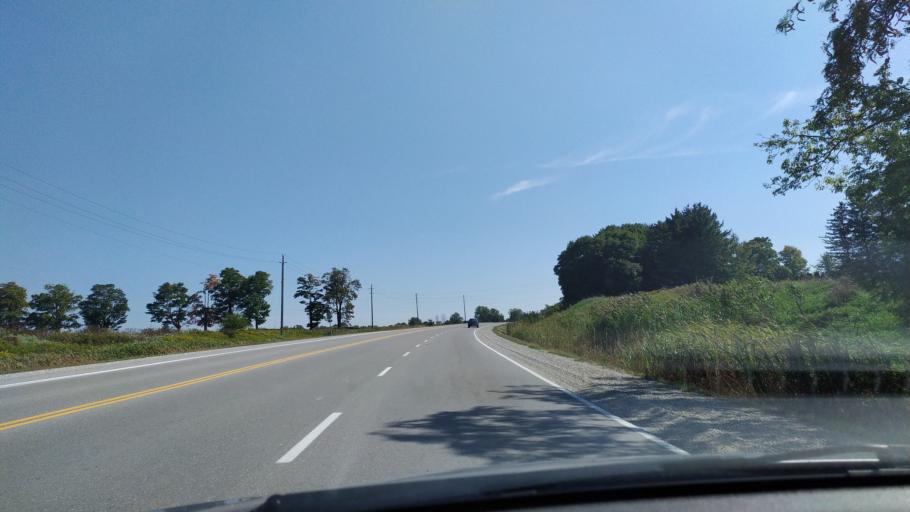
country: CA
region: Ontario
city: Ingersoll
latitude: 43.0653
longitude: -80.8411
